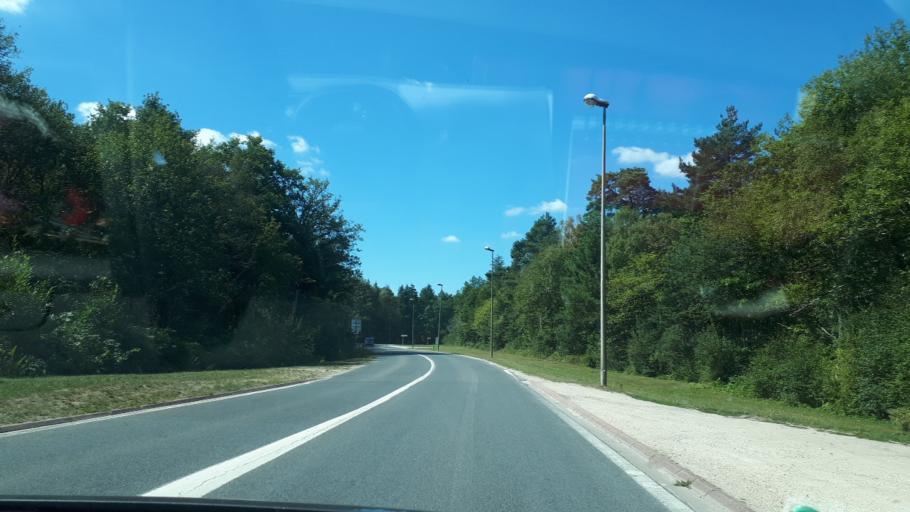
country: FR
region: Centre
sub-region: Departement du Loir-et-Cher
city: Lamotte-Beuvron
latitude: 47.5940
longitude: 2.0152
